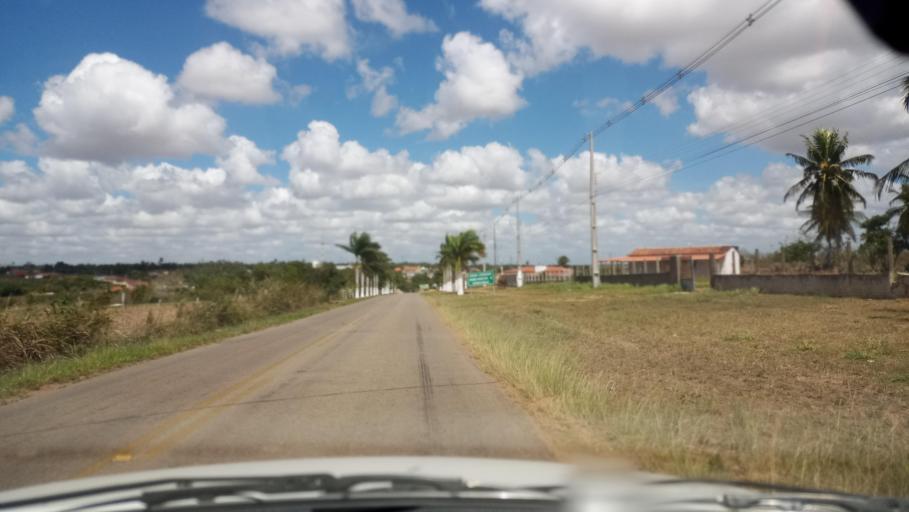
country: BR
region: Rio Grande do Norte
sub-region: Brejinho
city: Brejinho
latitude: -6.0420
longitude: -35.4221
